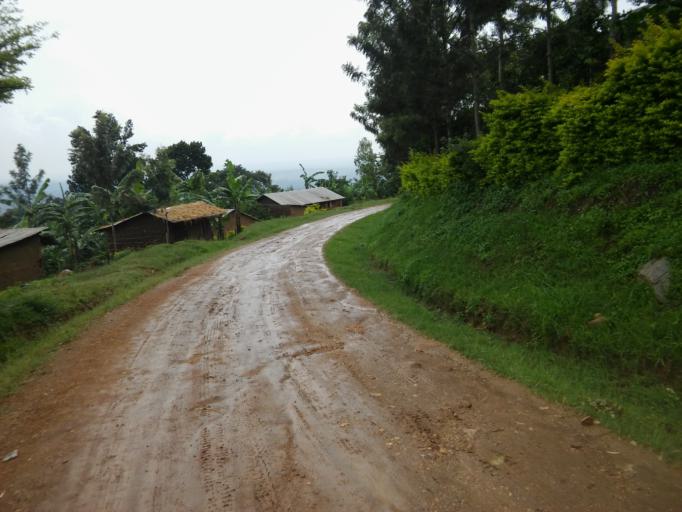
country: UG
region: Eastern Region
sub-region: Mbale District
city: Mbale
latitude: 1.0158
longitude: 34.2218
